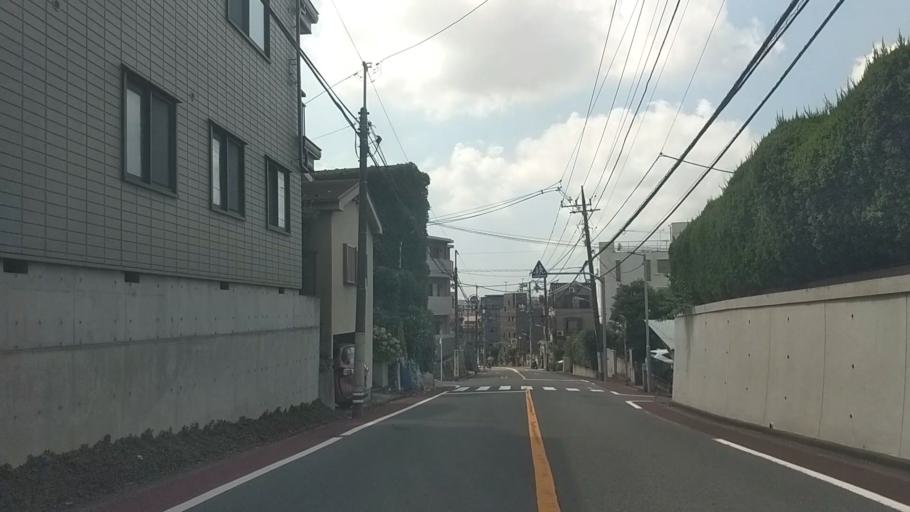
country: JP
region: Kanagawa
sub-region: Kawasaki-shi
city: Kawasaki
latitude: 35.5845
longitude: 139.7162
